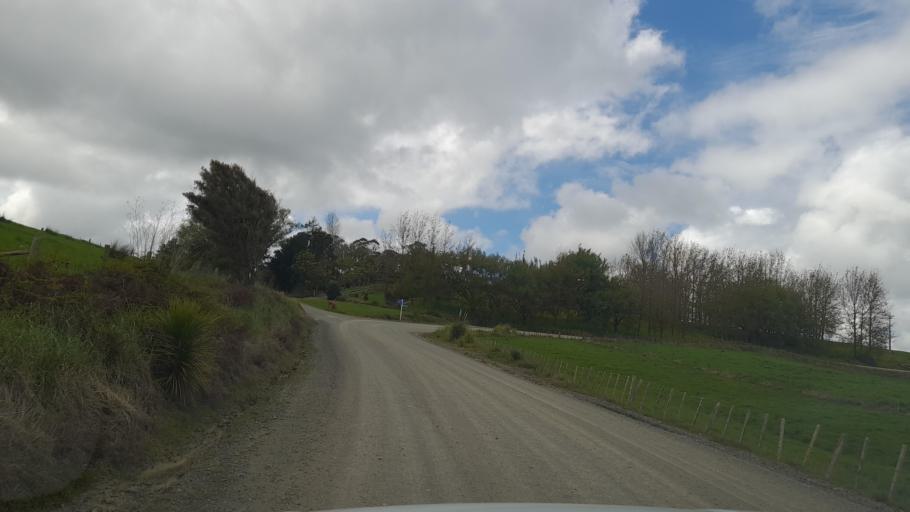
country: NZ
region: Auckland
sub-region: Auckland
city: Wellsford
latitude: -36.1651
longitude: 174.3200
